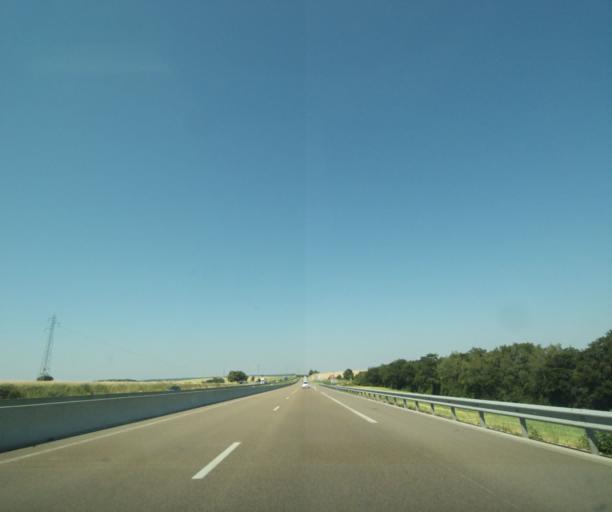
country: FR
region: Lorraine
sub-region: Departement de la Meuse
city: Ligny-en-Barrois
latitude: 48.6970
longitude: 5.3772
